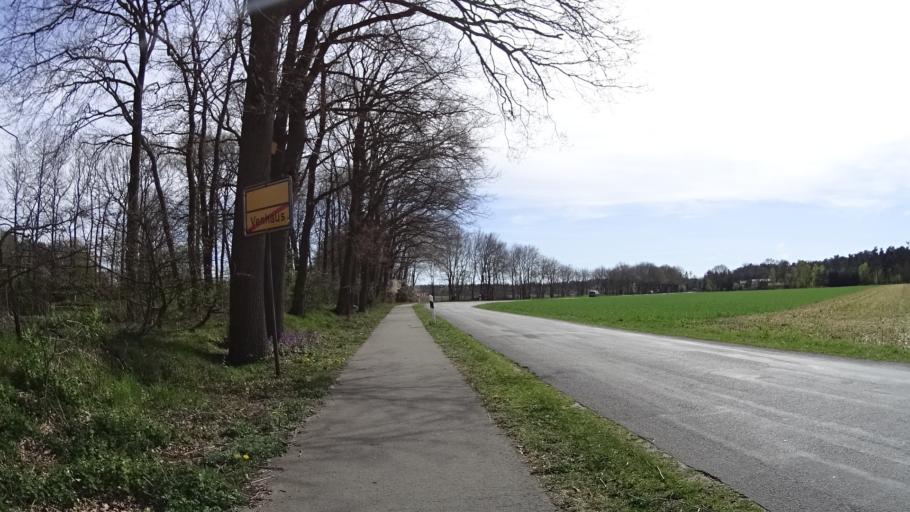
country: DE
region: Lower Saxony
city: Spelle
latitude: 52.3547
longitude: 7.4445
